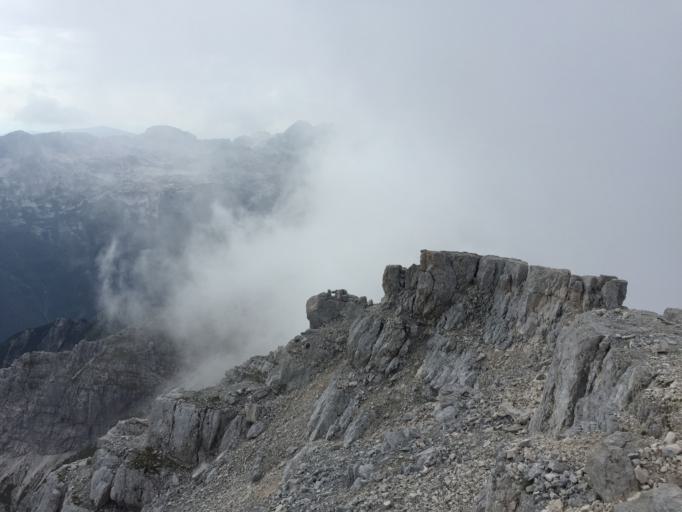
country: IT
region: Friuli Venezia Giulia
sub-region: Provincia di Udine
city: Malborghetto
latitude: 46.4294
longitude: 13.4906
